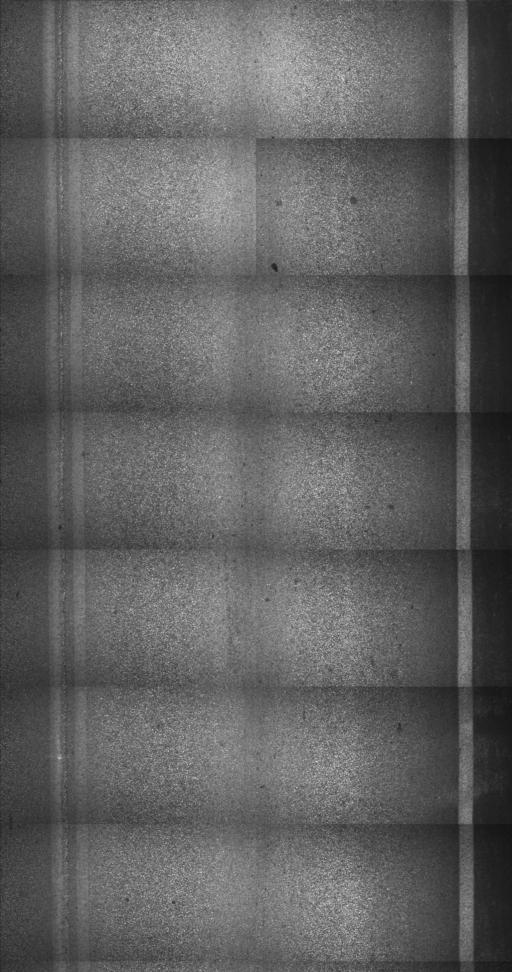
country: US
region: Vermont
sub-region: Rutland County
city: Rutland
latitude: 43.7446
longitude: -72.8204
